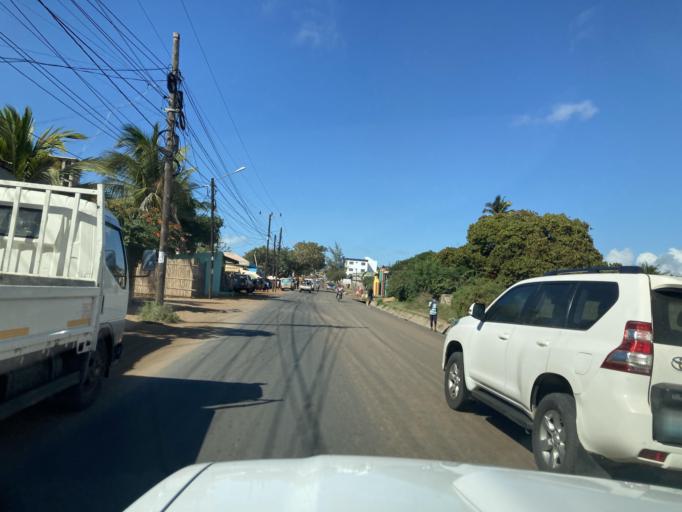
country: MZ
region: Cabo Delgado
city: Pemba
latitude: -12.9786
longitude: 40.5414
